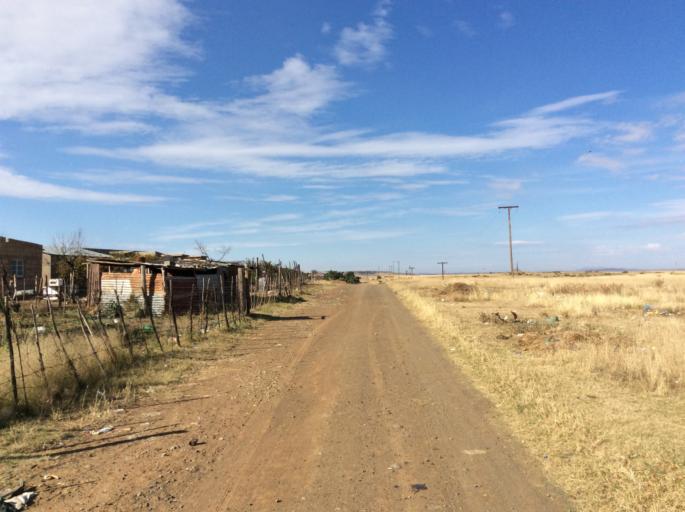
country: LS
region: Mafeteng
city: Mafeteng
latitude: -29.7161
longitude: 27.0106
